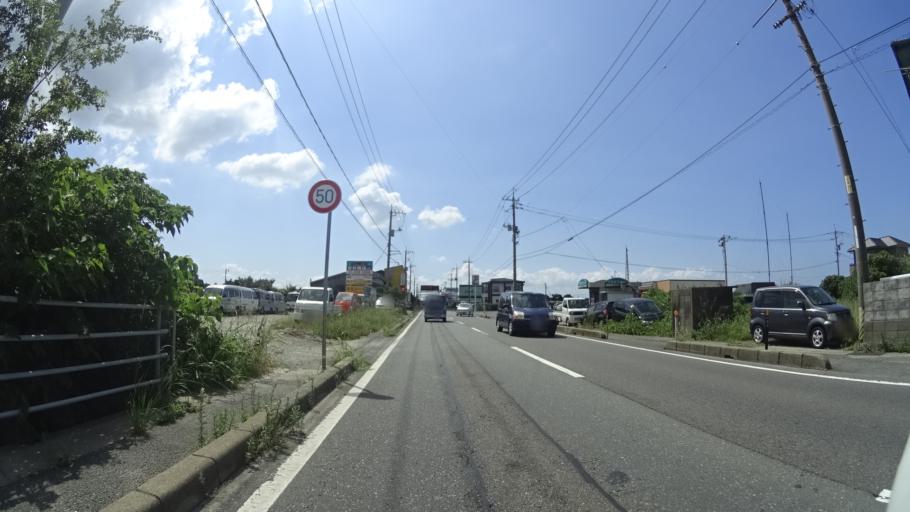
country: JP
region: Yamaguchi
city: Shimonoseki
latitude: 34.0393
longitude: 130.9142
